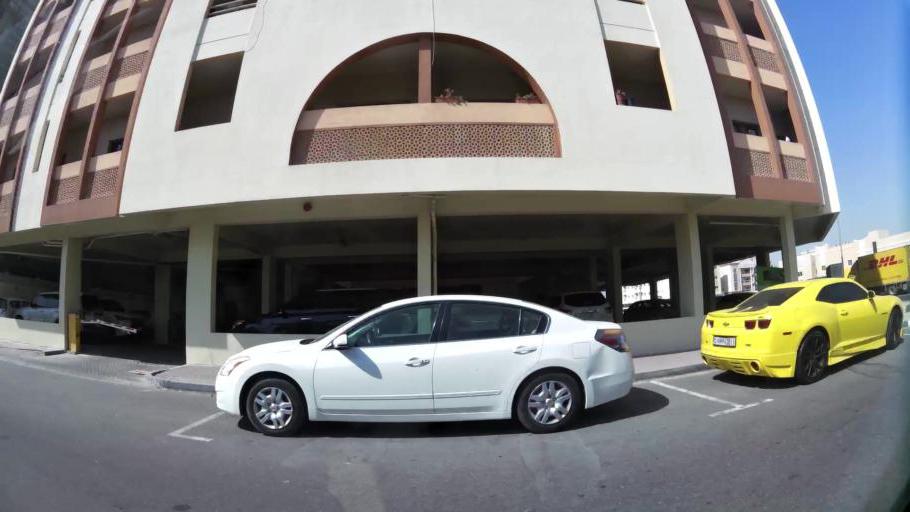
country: AE
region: Ash Shariqah
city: Sharjah
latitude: 25.2790
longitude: 55.3736
